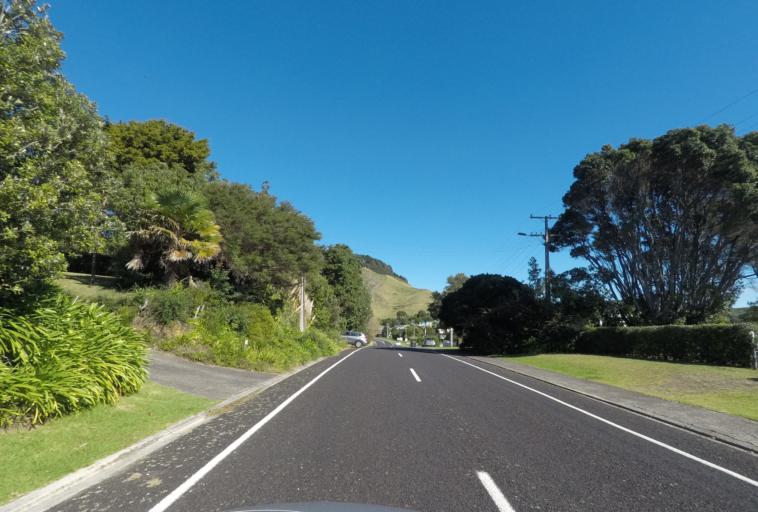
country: NZ
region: Waikato
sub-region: Thames-Coromandel District
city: Whangamata
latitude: -37.2834
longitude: 175.8993
